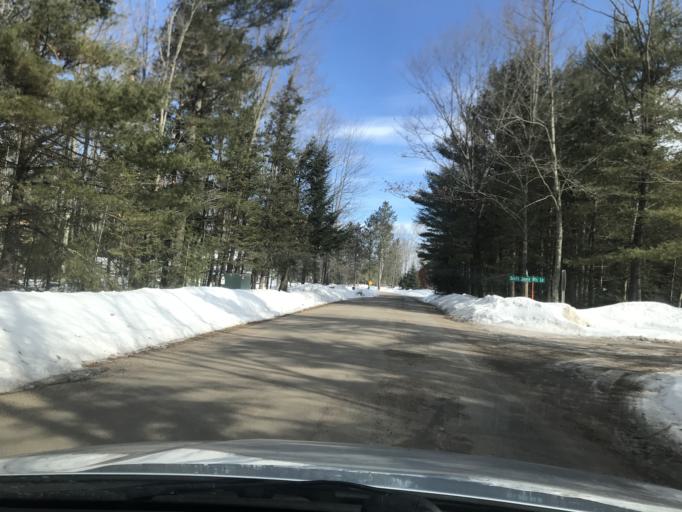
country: US
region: Wisconsin
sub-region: Menominee County
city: Legend Lake
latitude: 45.1207
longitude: -88.4460
